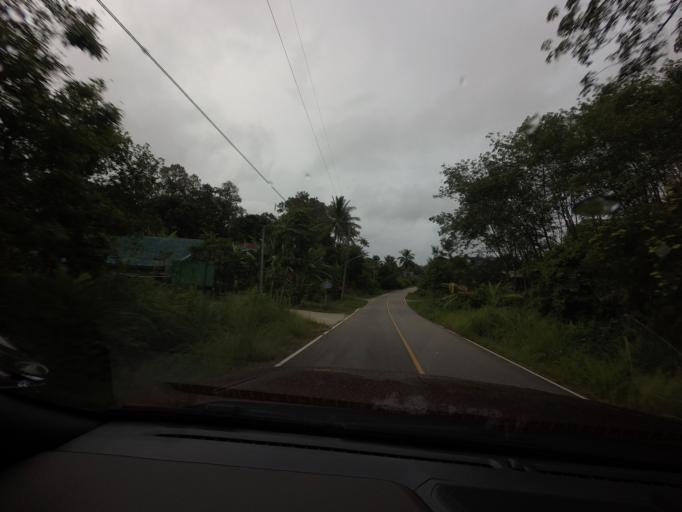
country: TH
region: Narathiwat
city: Chanae
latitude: 6.0345
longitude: 101.6915
